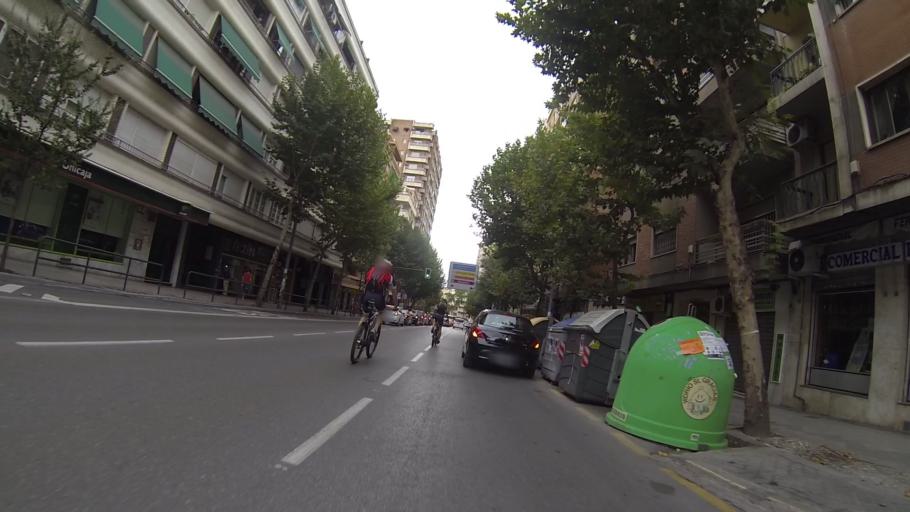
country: ES
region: Andalusia
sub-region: Provincia de Granada
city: Granada
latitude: 37.1874
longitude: -3.6077
